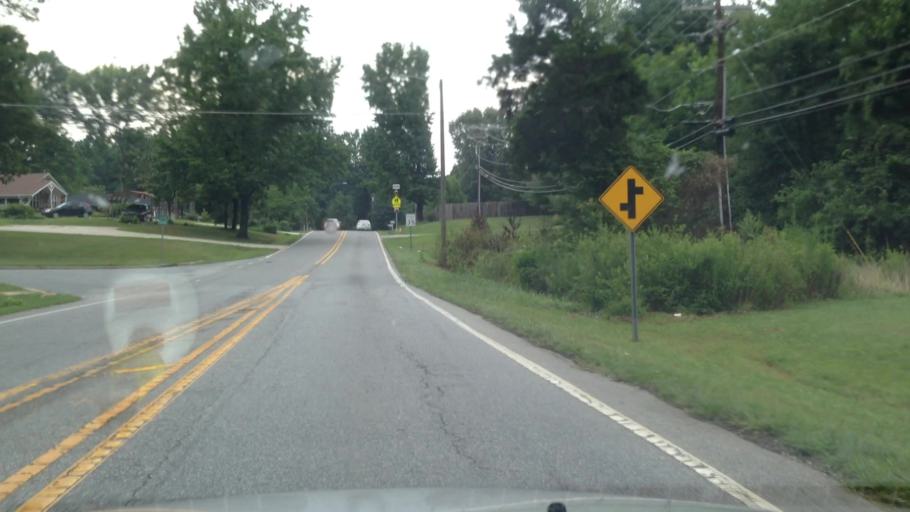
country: US
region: North Carolina
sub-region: Forsyth County
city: Kernersville
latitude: 36.1314
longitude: -80.0709
